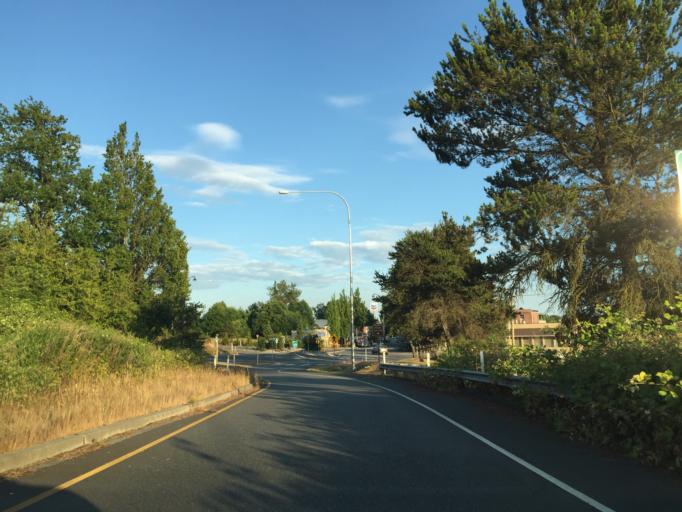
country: US
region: Washington
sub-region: Whatcom County
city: Blaine
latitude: 48.9979
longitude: -122.7533
